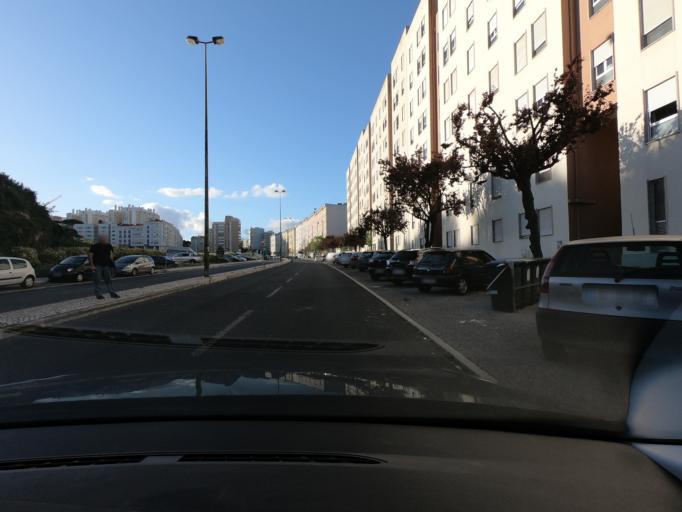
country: PT
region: Lisbon
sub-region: Lisbon
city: Lisbon
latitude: 38.7245
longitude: -9.1220
